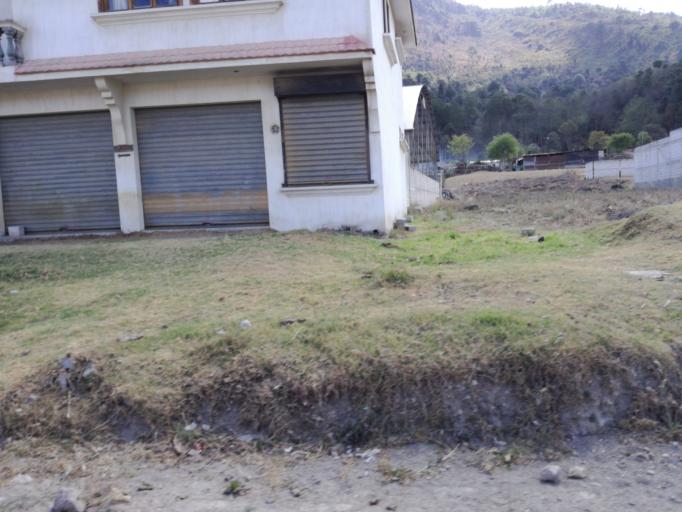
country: GT
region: Quetzaltenango
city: Almolonga
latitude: 14.7943
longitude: -91.5372
